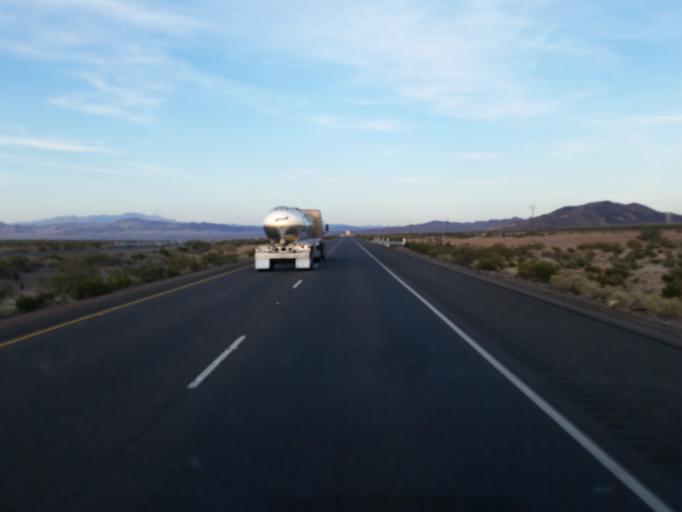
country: US
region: California
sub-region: San Bernardino County
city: Joshua Tree
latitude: 34.7289
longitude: -116.2650
